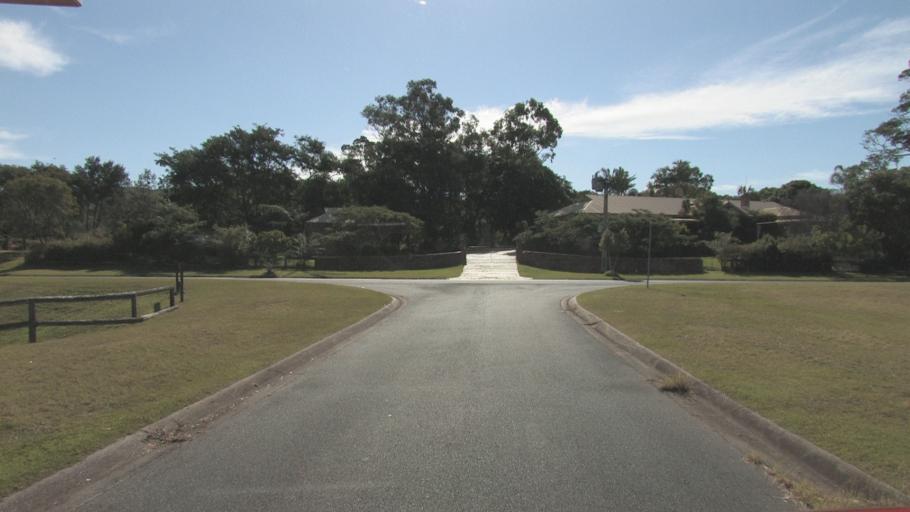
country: AU
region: Queensland
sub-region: Logan
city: Windaroo
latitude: -27.7584
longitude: 153.1815
